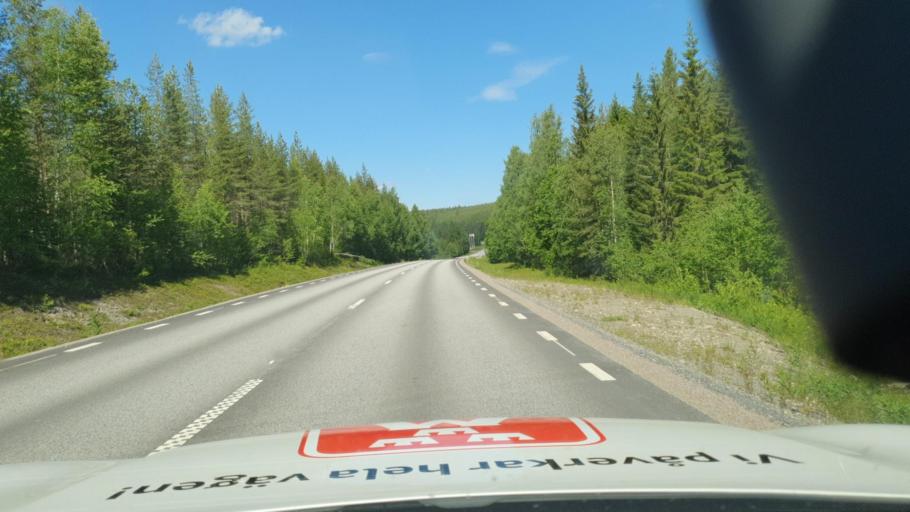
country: SE
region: Vaesterbotten
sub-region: Skelleftea Kommun
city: Boliden
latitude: 64.8909
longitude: 20.3768
